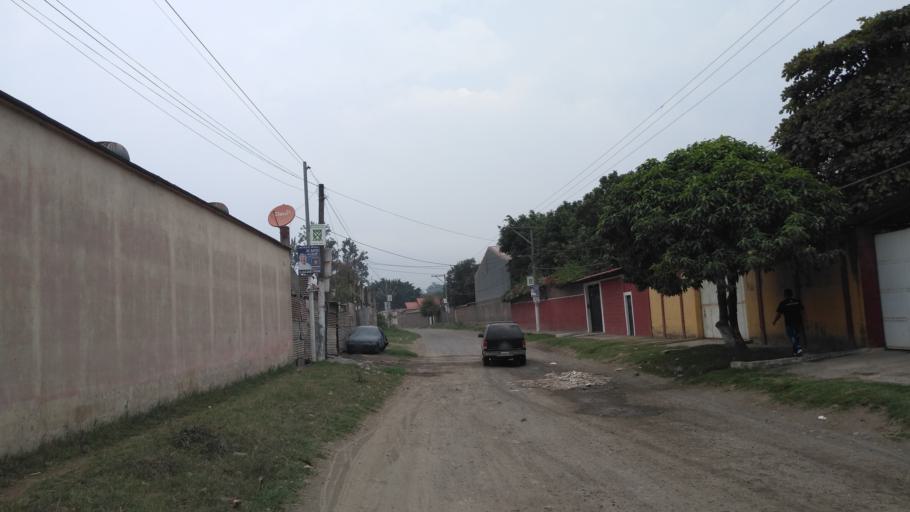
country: GT
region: Guatemala
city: Petapa
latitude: 14.5089
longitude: -90.5546
